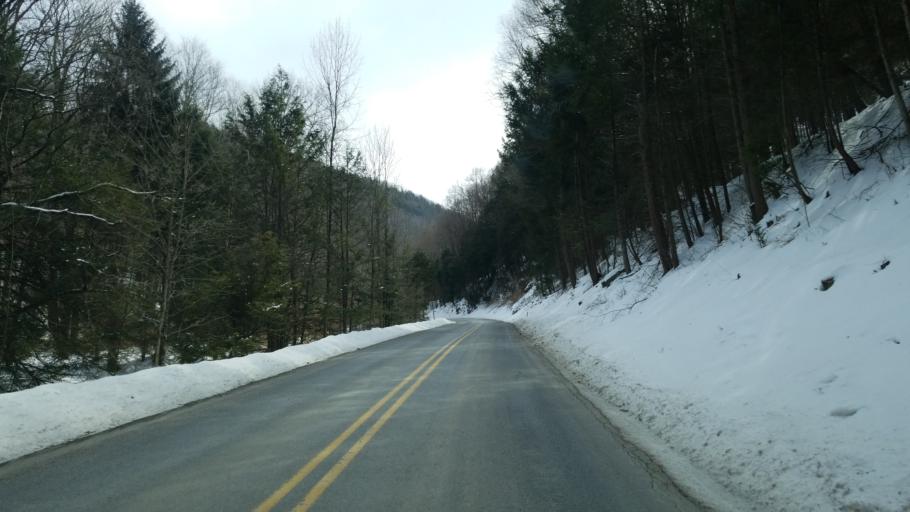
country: US
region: Pennsylvania
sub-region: Clearfield County
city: Shiloh
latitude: 41.2631
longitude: -78.1544
